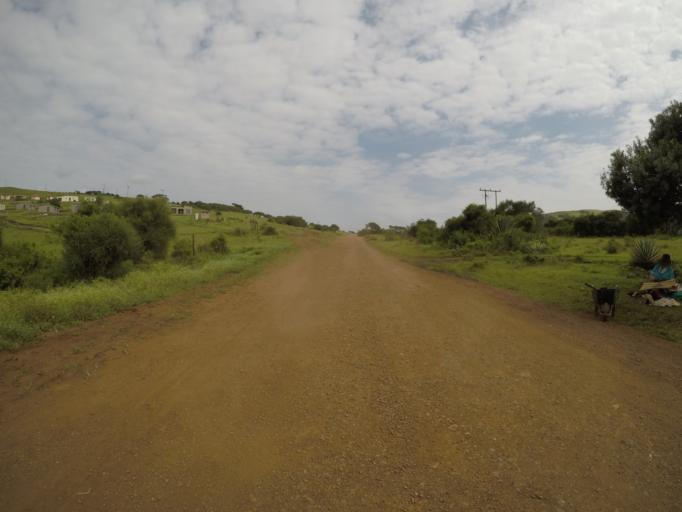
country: ZA
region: KwaZulu-Natal
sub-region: uThungulu District Municipality
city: Empangeni
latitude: -28.6165
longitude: 31.9015
